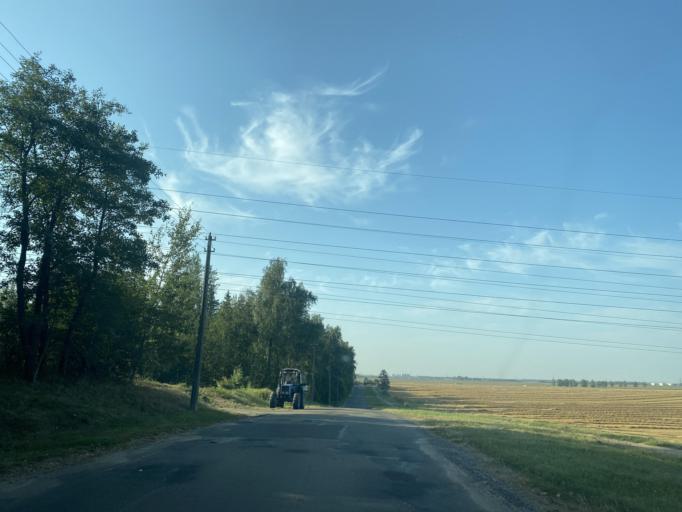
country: BY
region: Minsk
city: Hatava
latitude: 53.8324
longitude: 27.6388
